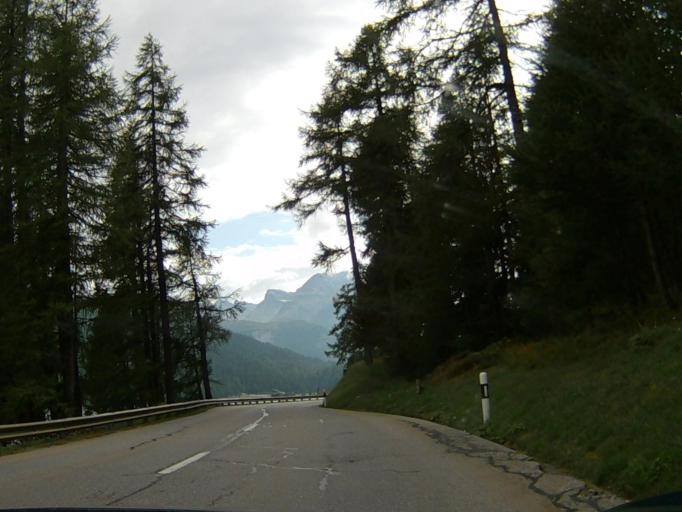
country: CH
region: Grisons
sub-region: Maloja District
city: Silvaplana
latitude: 46.4483
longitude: 9.7834
